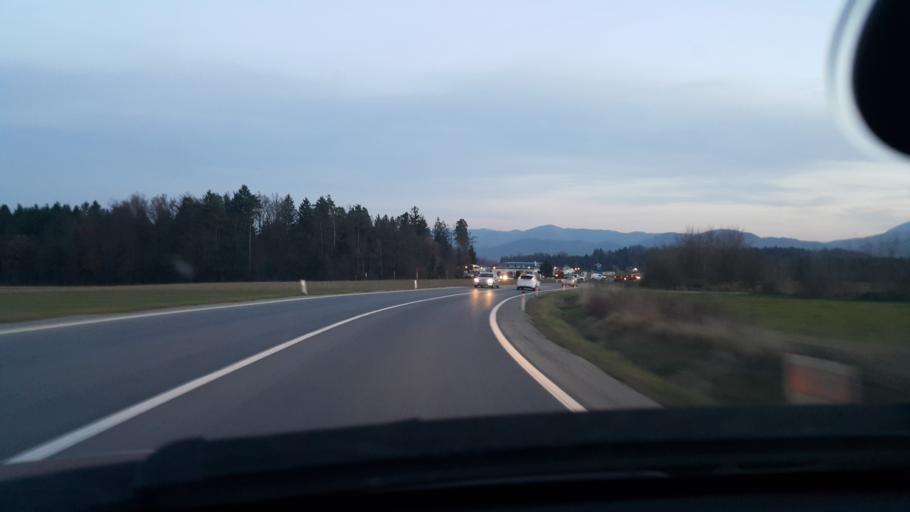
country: SI
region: Zalec
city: Gotovlje
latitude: 46.2788
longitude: 15.1846
